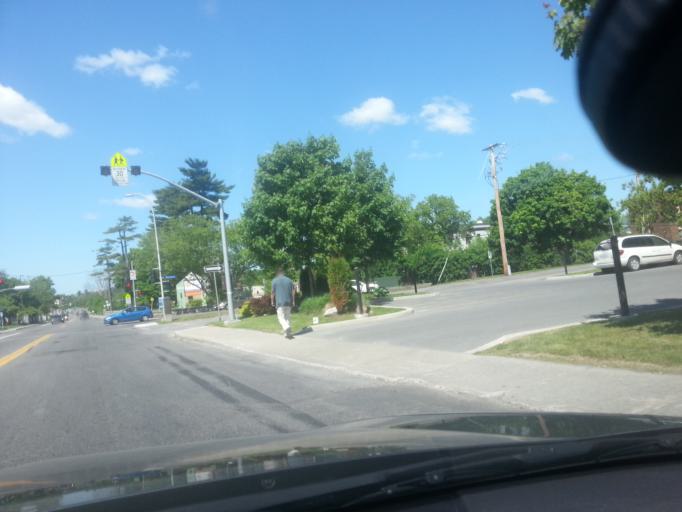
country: CA
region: Ontario
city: Ottawa
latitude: 45.4215
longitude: -75.7469
